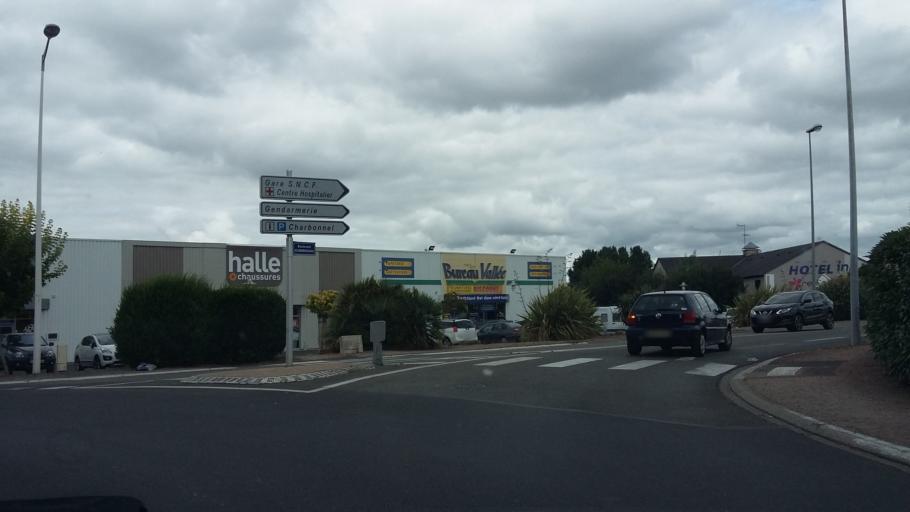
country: FR
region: Pays de la Loire
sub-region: Departement de la Vendee
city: Challans
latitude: 46.8510
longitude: -1.8898
